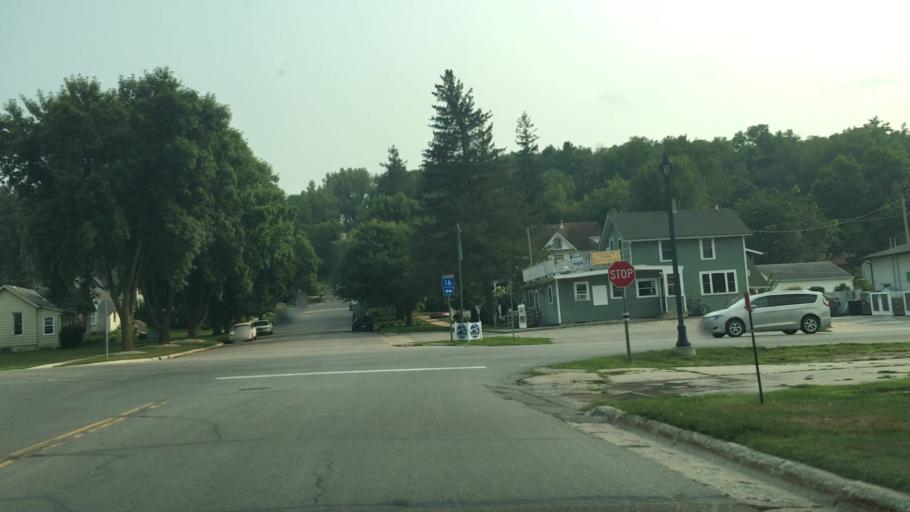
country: US
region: Minnesota
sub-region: Fillmore County
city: Preston
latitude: 43.7143
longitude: -91.9770
